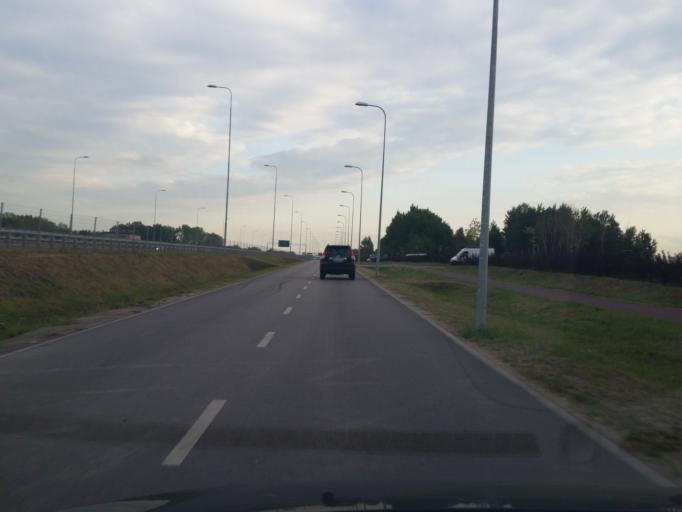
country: PL
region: Masovian Voivodeship
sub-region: Warszawa
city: Wlochy
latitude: 52.1546
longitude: 20.9871
